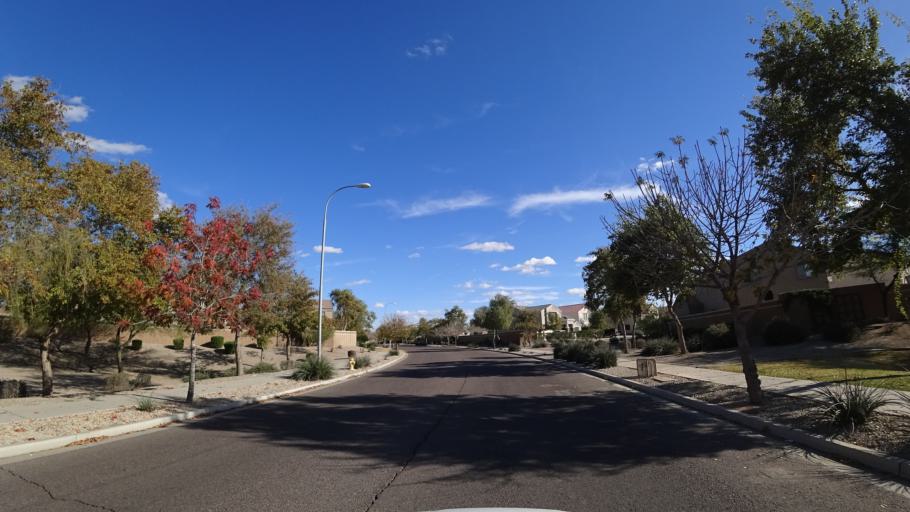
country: US
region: Arizona
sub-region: Maricopa County
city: Tolleson
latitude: 33.4201
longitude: -112.2466
